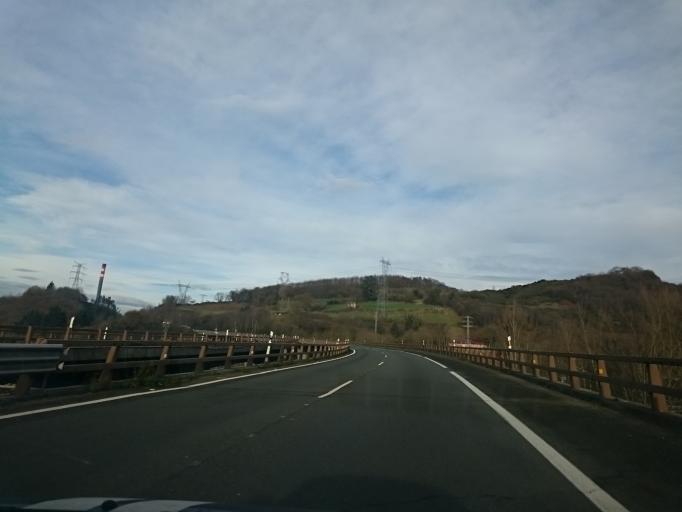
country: ES
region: Asturias
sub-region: Province of Asturias
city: Castandiello
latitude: 43.3097
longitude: -5.8629
